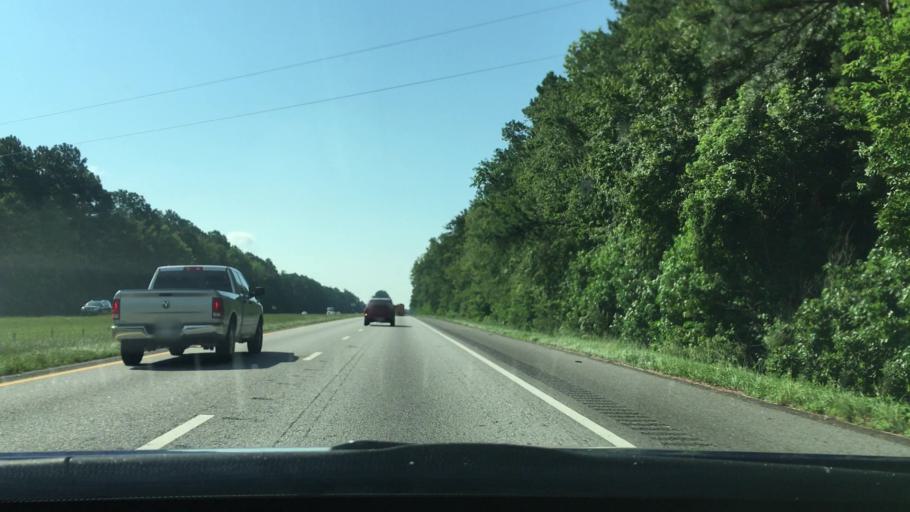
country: US
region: South Carolina
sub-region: Dorchester County
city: Ridgeville
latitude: 33.1805
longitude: -80.3779
